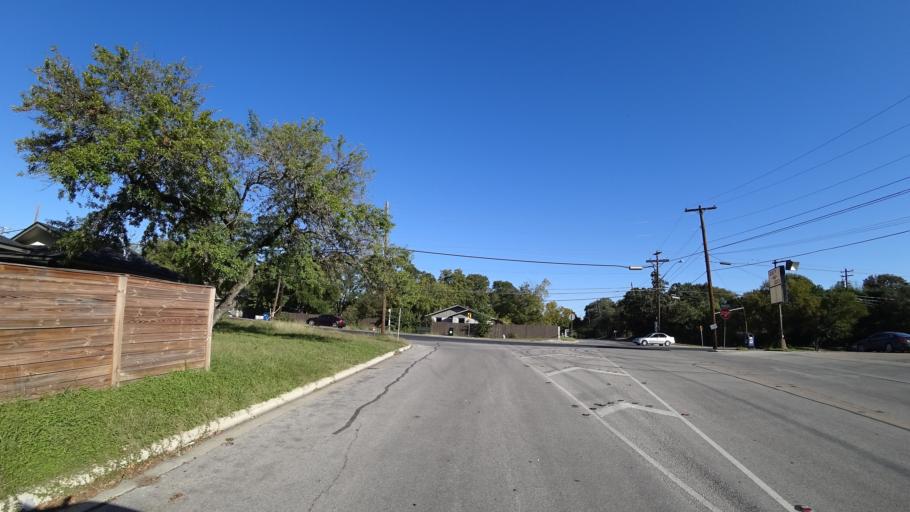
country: US
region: Texas
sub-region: Travis County
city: Austin
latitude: 30.3077
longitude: -97.6763
